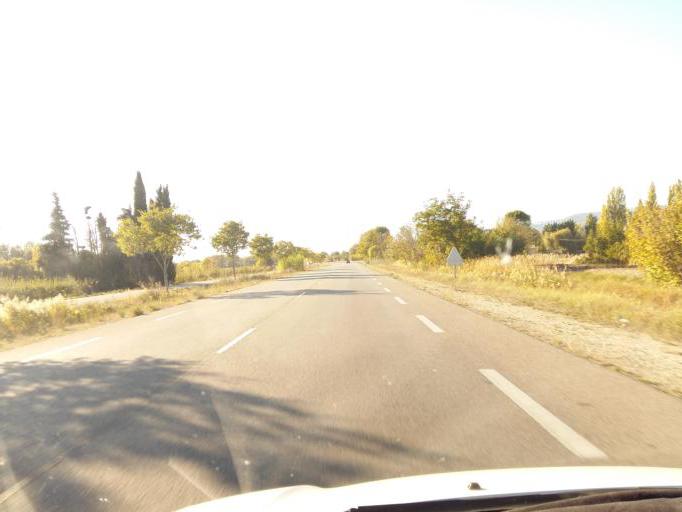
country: FR
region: Provence-Alpes-Cote d'Azur
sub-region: Departement du Vaucluse
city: Cadenet
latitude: 43.7344
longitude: 5.3498
